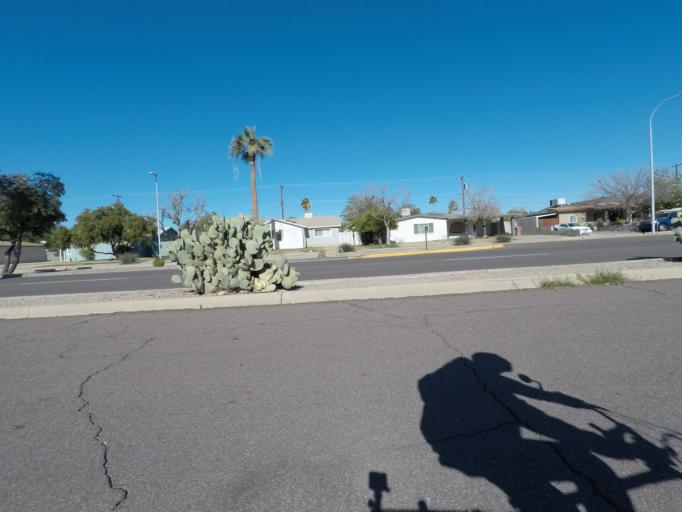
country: US
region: Arizona
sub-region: Maricopa County
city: Tempe
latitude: 33.4511
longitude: -111.9232
